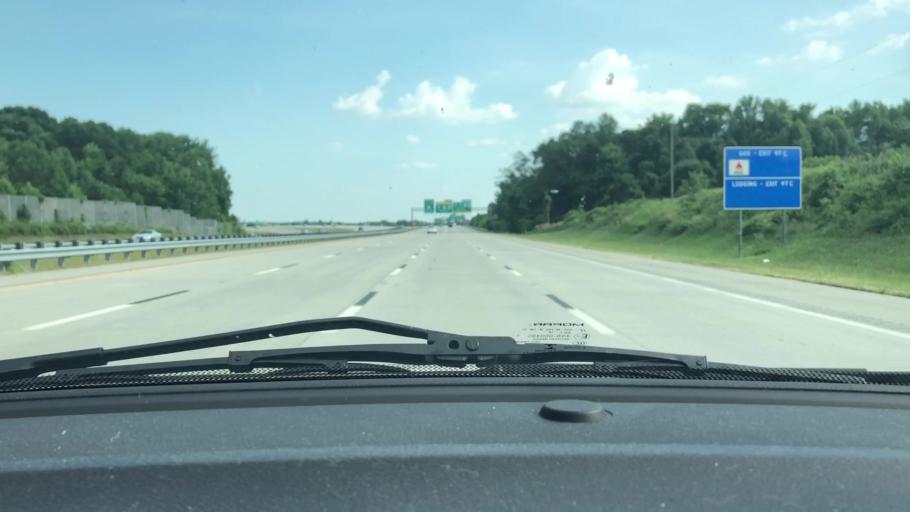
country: US
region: North Carolina
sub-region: Guilford County
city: Jamestown
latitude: 36.0136
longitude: -79.8533
